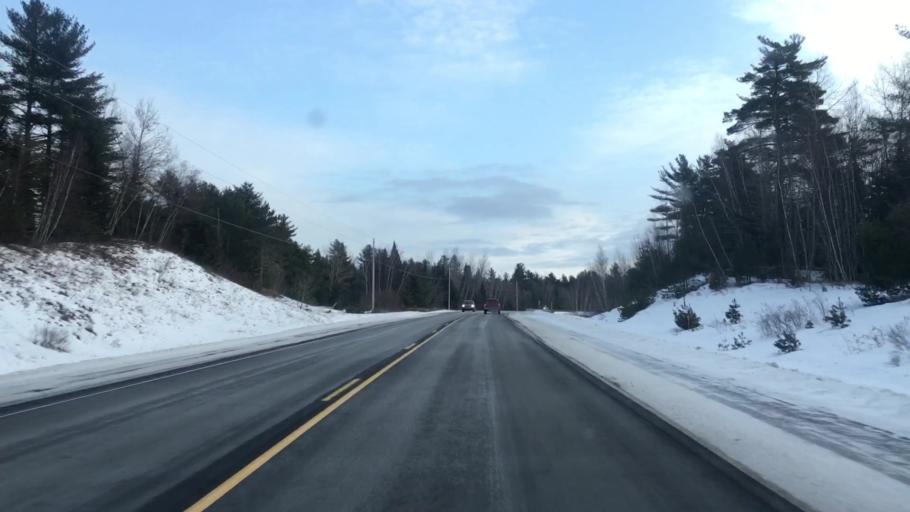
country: US
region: Maine
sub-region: Washington County
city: Addison
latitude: 44.9389
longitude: -67.7317
